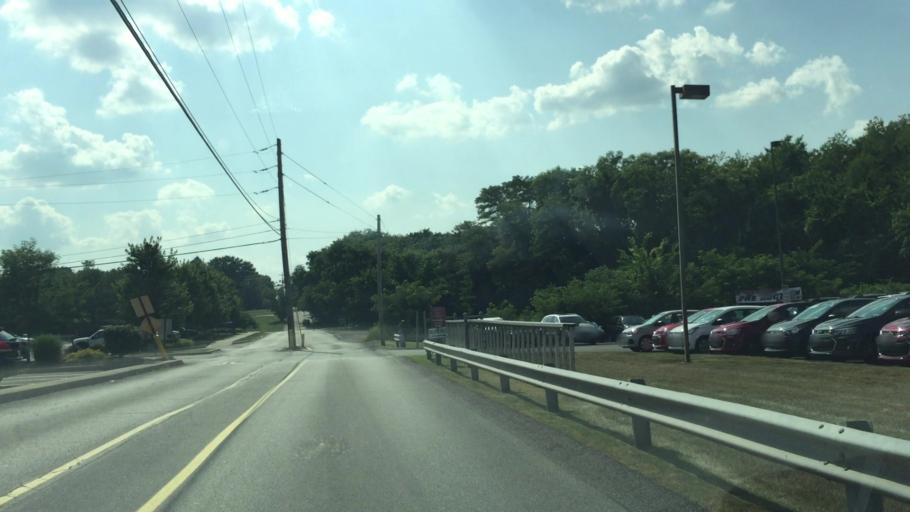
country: US
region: Pennsylvania
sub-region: Allegheny County
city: Carnot-Moon
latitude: 40.5225
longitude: -80.2206
